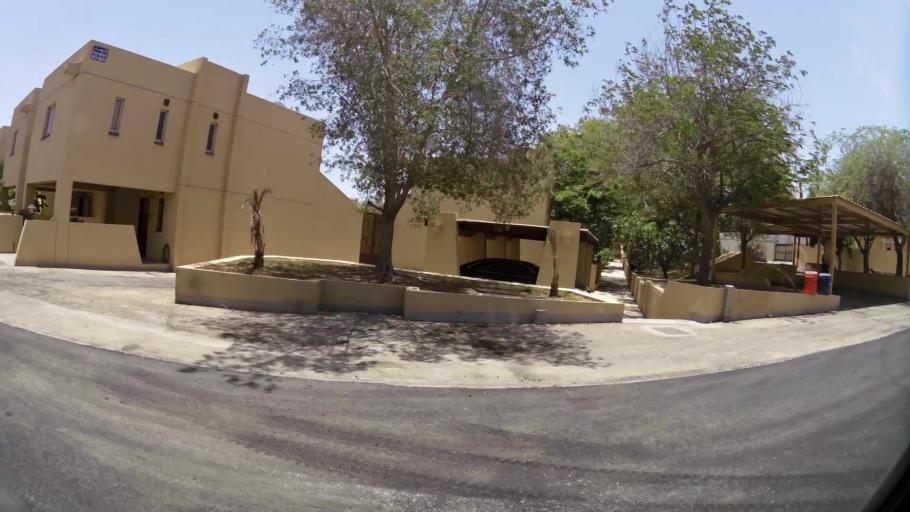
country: OM
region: Muhafazat Masqat
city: Bawshar
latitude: 23.6061
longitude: 58.4569
